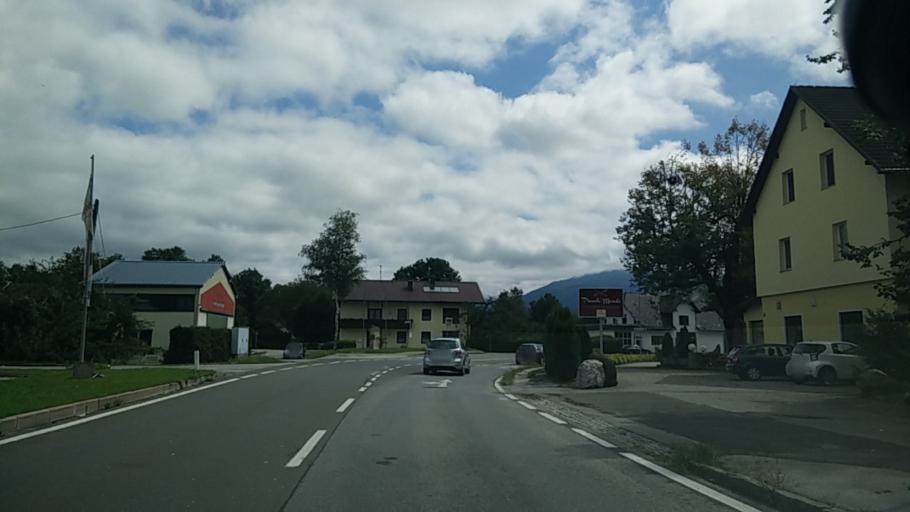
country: AT
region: Carinthia
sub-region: Politischer Bezirk Klagenfurt Land
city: Kottmannsdorf
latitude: 46.5390
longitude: 14.2583
